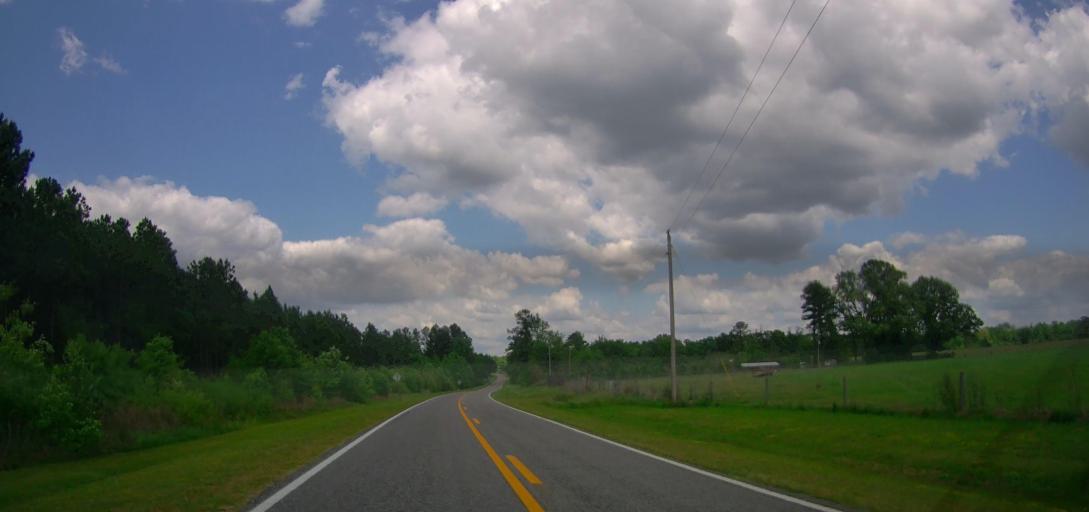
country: US
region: Georgia
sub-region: Laurens County
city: East Dublin
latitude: 32.5492
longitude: -82.8185
